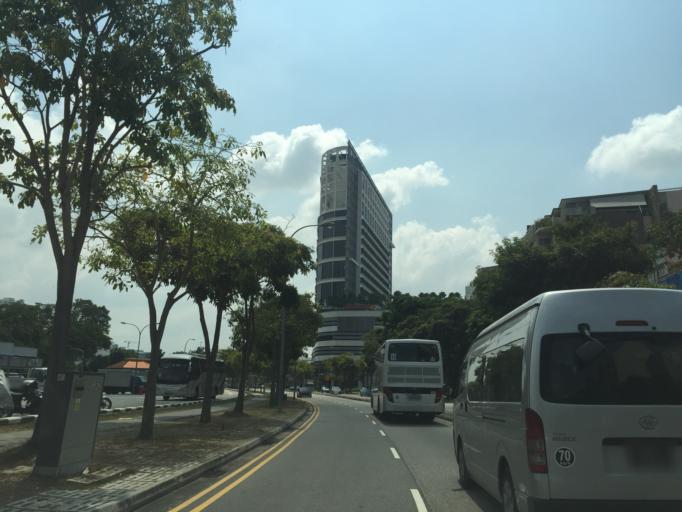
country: SG
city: Singapore
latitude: 1.3104
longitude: 103.8523
